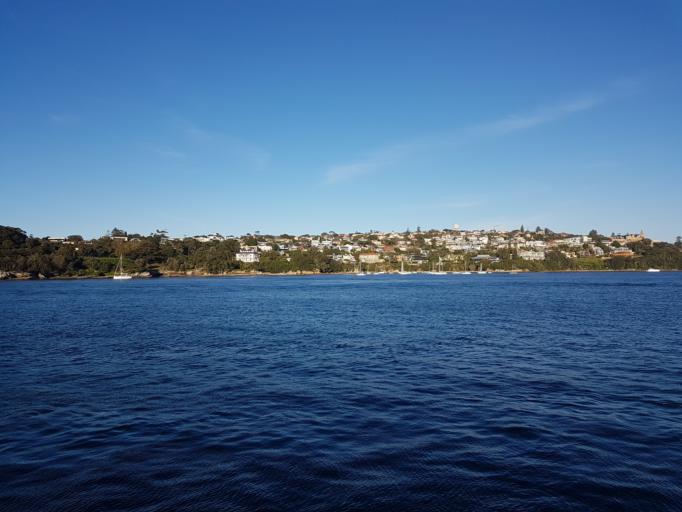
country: AU
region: New South Wales
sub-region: Woollahra
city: Point Piper
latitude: -33.8561
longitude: 151.2613
